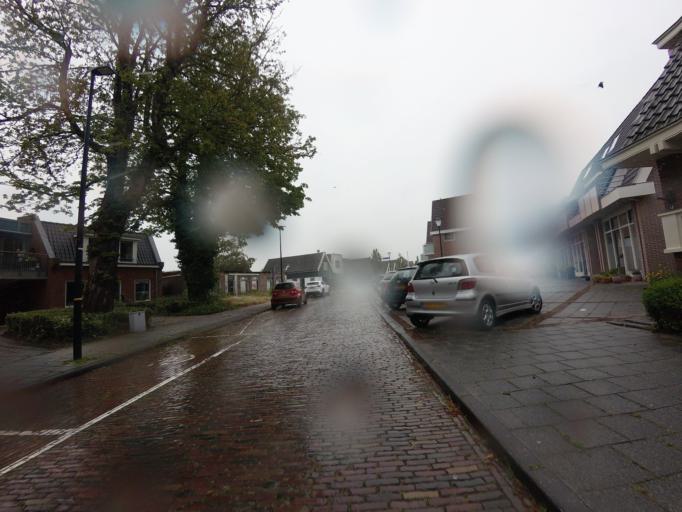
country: NL
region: North Holland
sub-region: Gemeente Schagen
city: Schagen
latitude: 52.7851
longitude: 4.8014
